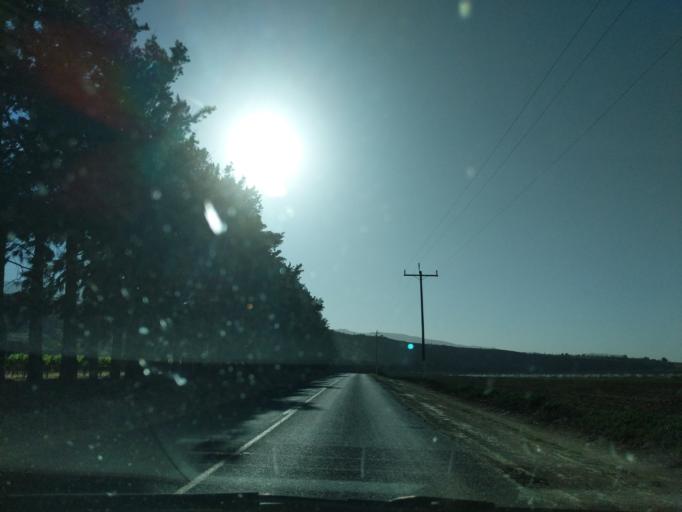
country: US
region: California
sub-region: Monterey County
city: Soledad
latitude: 36.4113
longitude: -121.3867
